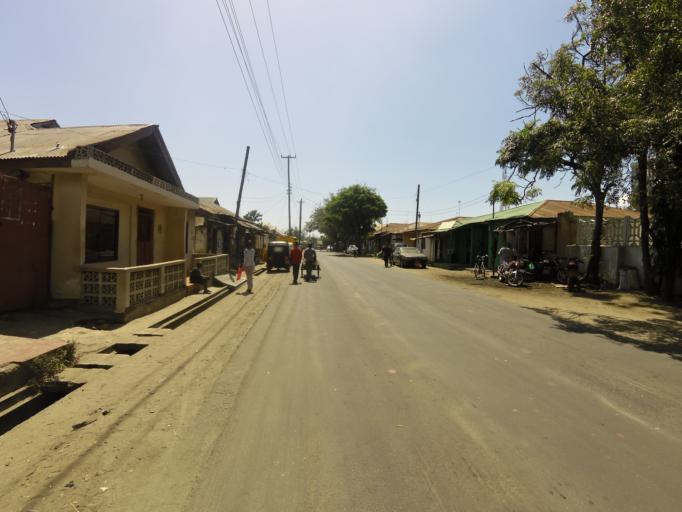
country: TZ
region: Dar es Salaam
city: Magomeni
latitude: -6.8006
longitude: 39.2522
